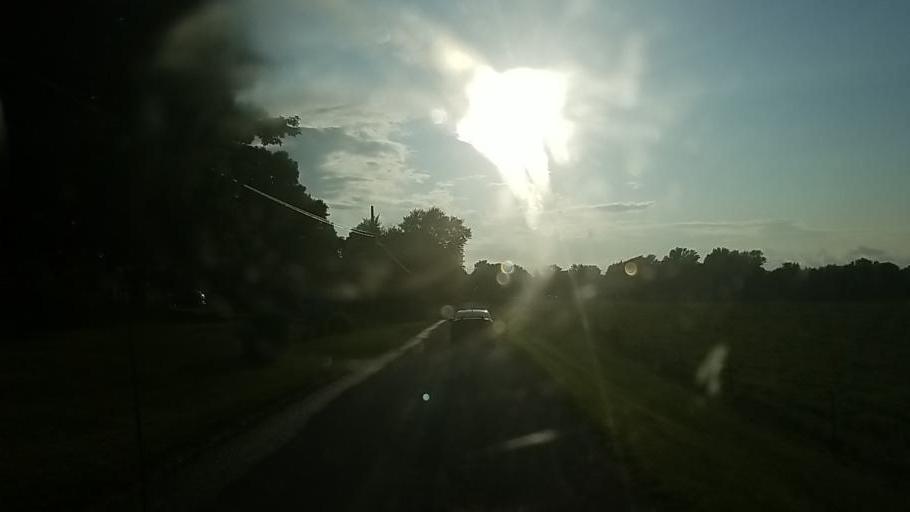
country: US
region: Ohio
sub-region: Crawford County
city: Galion
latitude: 40.6692
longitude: -82.8359
